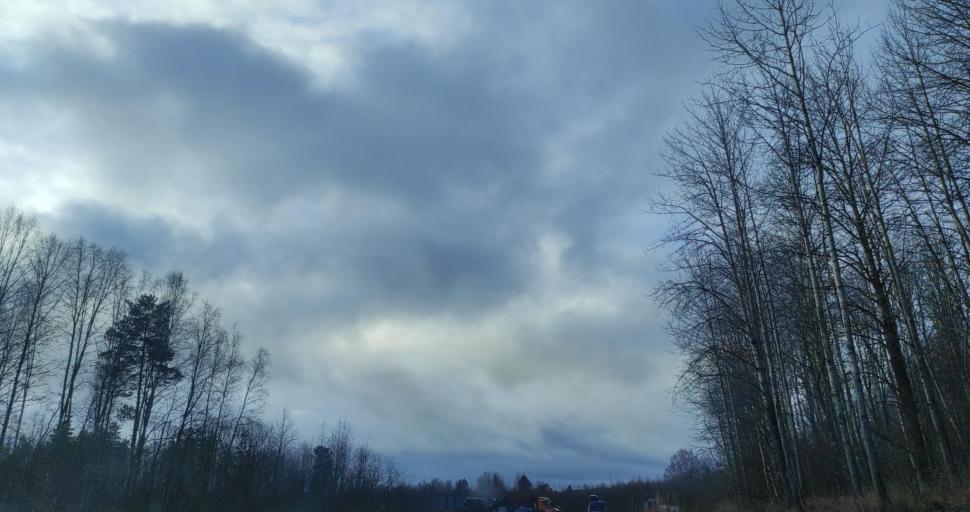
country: RU
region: Republic of Karelia
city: Pitkyaranta
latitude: 61.6982
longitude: 31.3152
